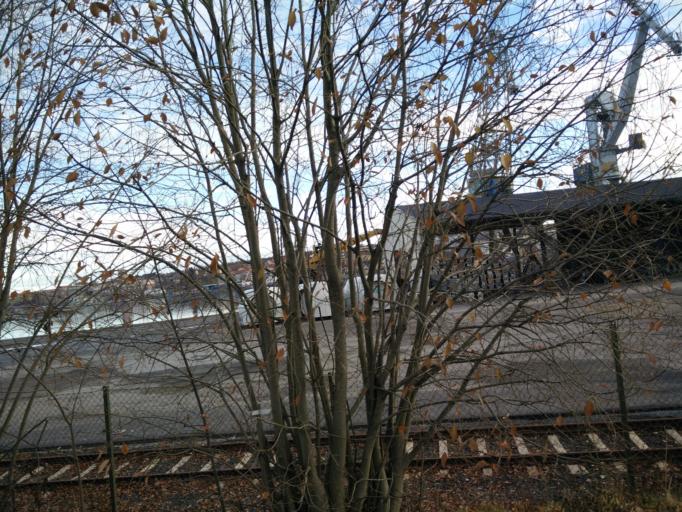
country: SE
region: Vaesternorrland
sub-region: Haernoesands Kommun
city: Haernoesand
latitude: 62.6391
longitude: 17.9342
